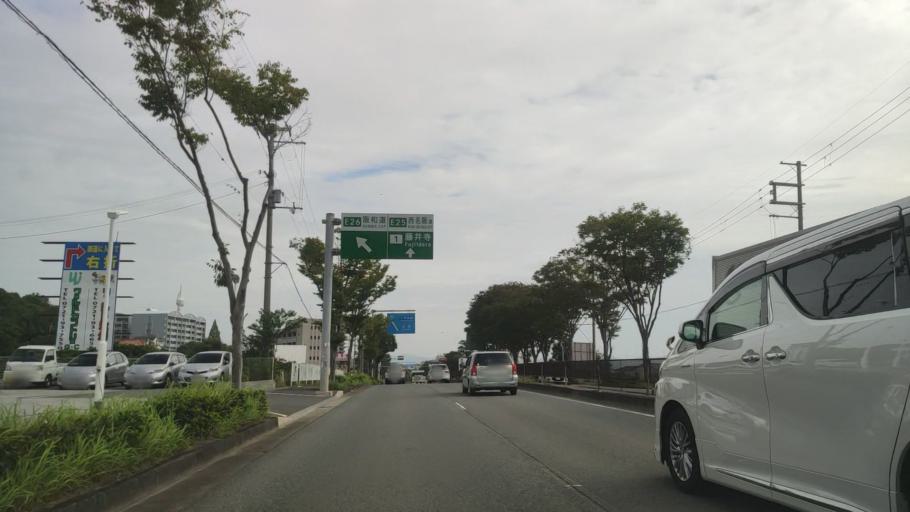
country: JP
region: Osaka
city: Tondabayashicho
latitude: 34.4880
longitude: 135.5821
